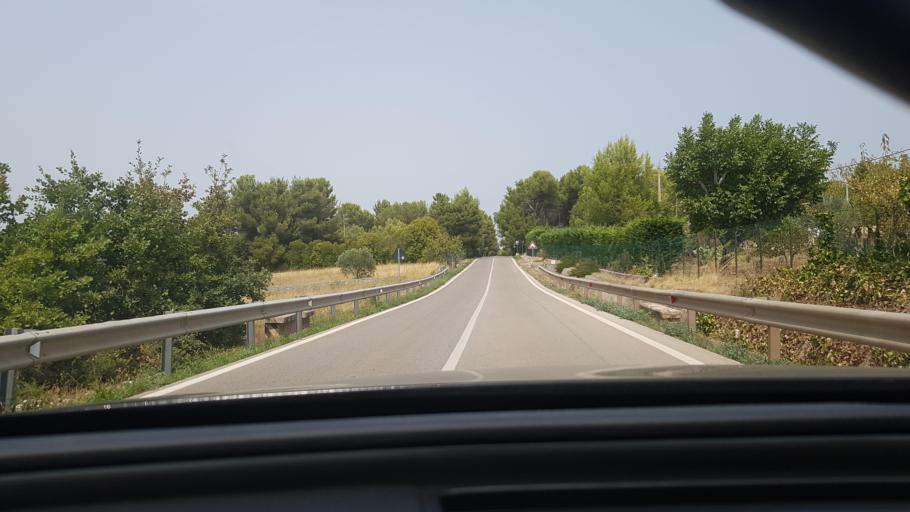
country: IT
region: Apulia
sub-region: Provincia di Barletta - Andria - Trani
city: Andria
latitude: 41.1242
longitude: 16.2871
